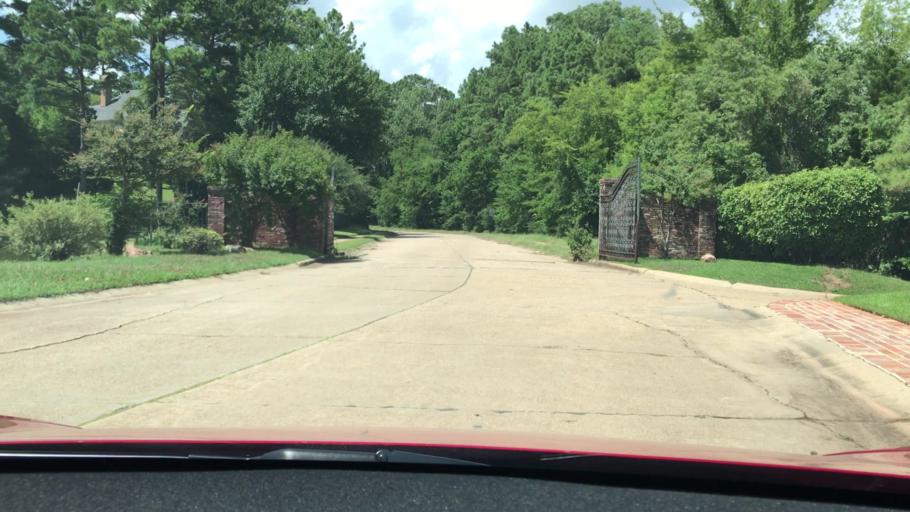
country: US
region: Louisiana
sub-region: Bossier Parish
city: Bossier City
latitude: 32.4208
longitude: -93.7286
